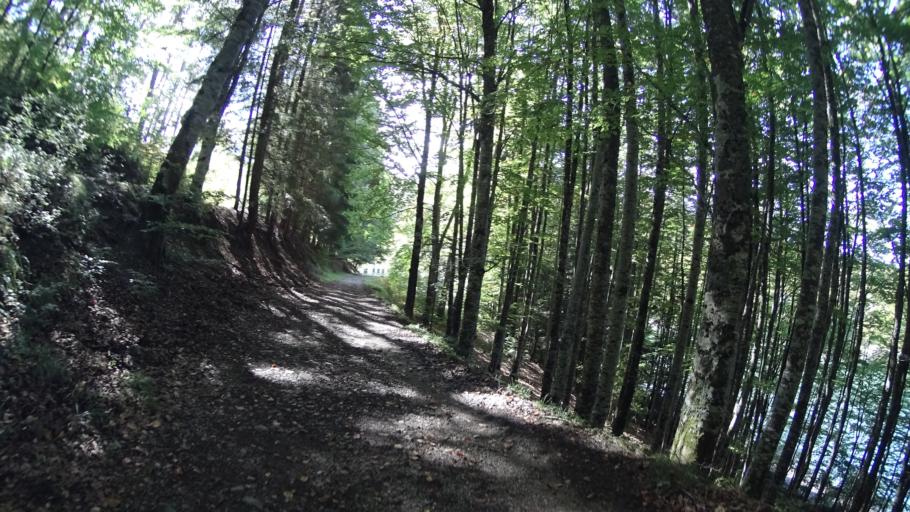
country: ES
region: Navarre
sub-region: Provincia de Navarra
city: Orbara
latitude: 42.9895
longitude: -1.1379
